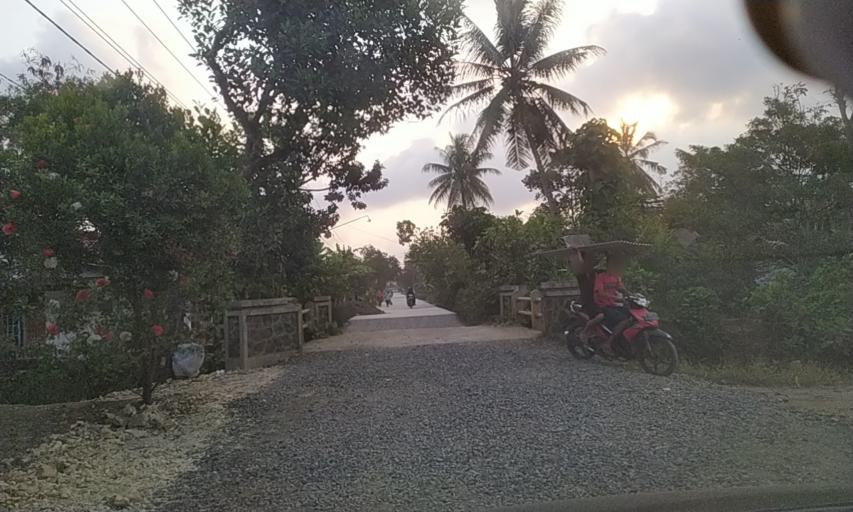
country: ID
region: Central Java
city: Bantarsari Kulon
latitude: -7.6007
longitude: 109.1011
